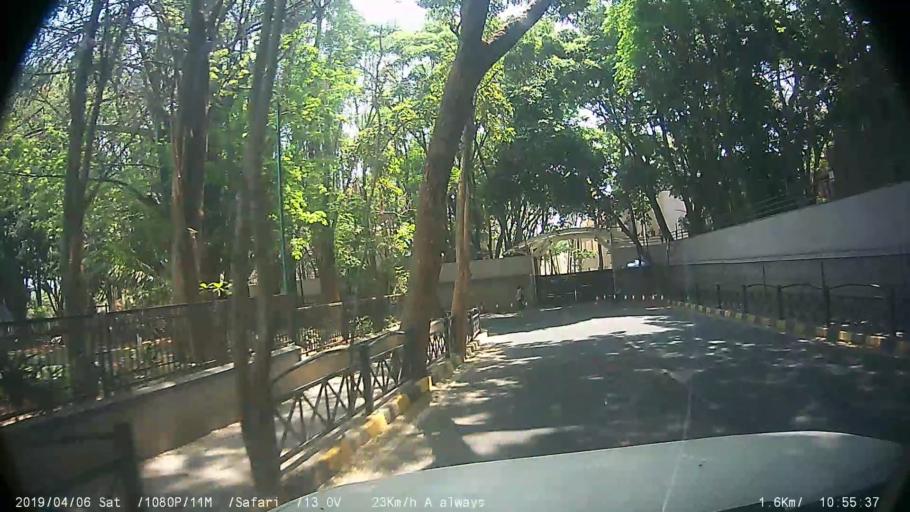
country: IN
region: Karnataka
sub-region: Bangalore Urban
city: Anekal
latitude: 12.8472
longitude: 77.6618
